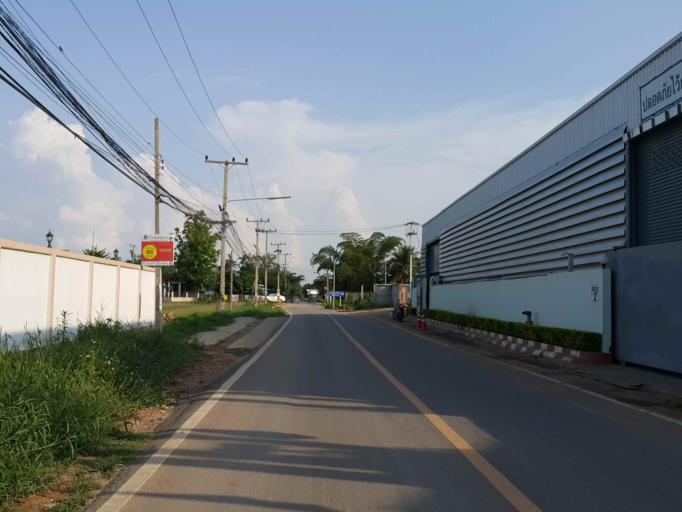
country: TH
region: Chiang Mai
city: San Sai
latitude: 18.8366
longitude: 99.0808
